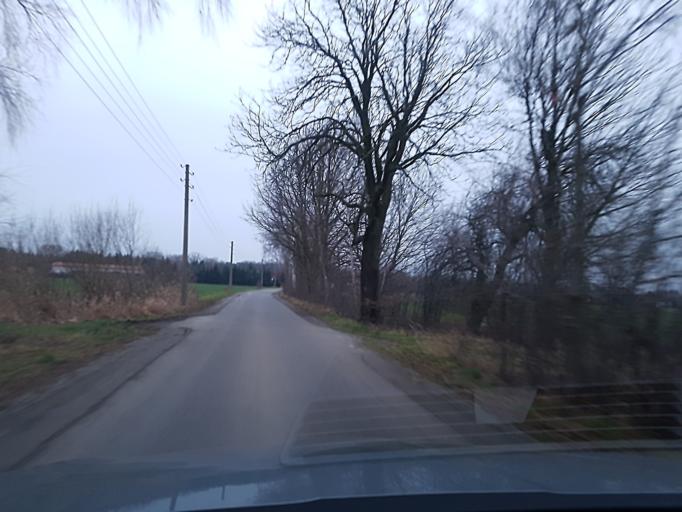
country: DE
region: Brandenburg
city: Schonewalde
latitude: 51.6412
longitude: 13.6114
